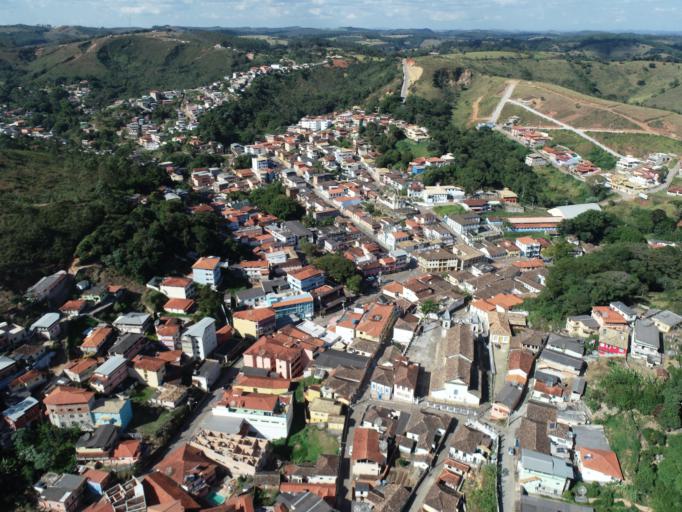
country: BR
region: Minas Gerais
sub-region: Tiradentes
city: Tiradentes
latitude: -21.0570
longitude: -44.0816
